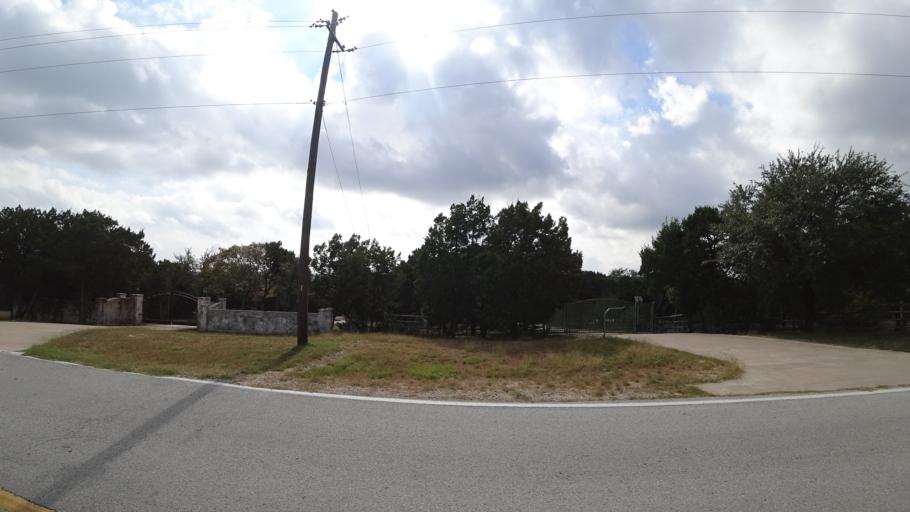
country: US
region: Texas
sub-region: Travis County
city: Barton Creek
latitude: 30.3030
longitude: -97.8771
